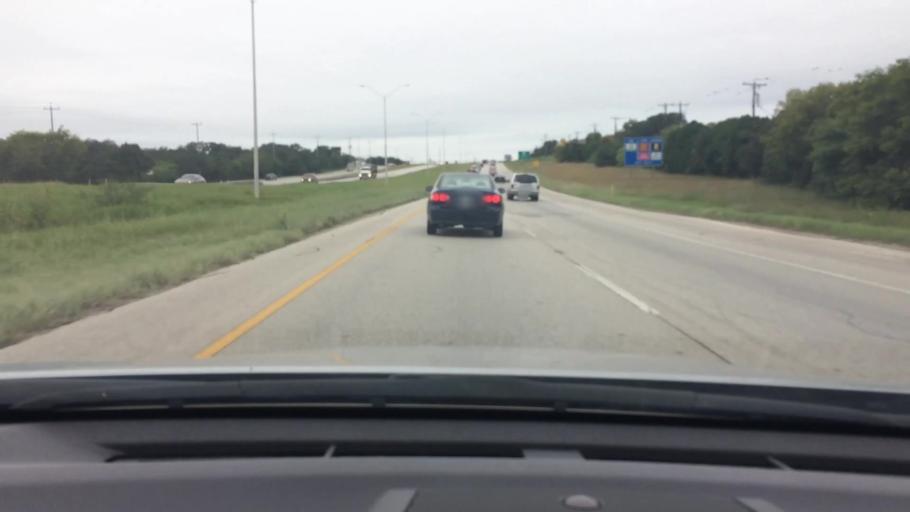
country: US
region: Texas
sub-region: Bexar County
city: Live Oak
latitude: 29.5506
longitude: -98.3203
